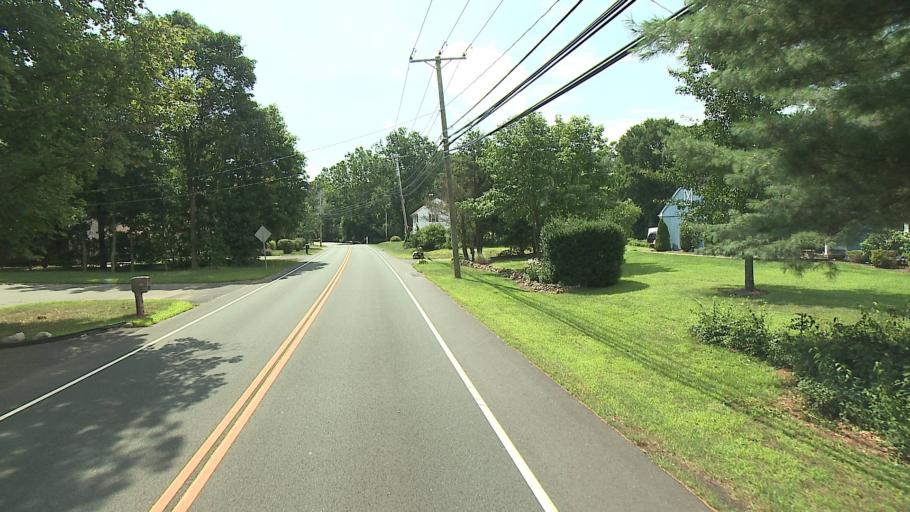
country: US
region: Connecticut
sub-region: Hartford County
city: Collinsville
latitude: 41.7826
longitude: -72.8925
